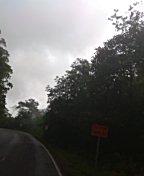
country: CR
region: San Jose
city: Dulce Nombre de Jesus
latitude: 10.0857
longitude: -83.9819
